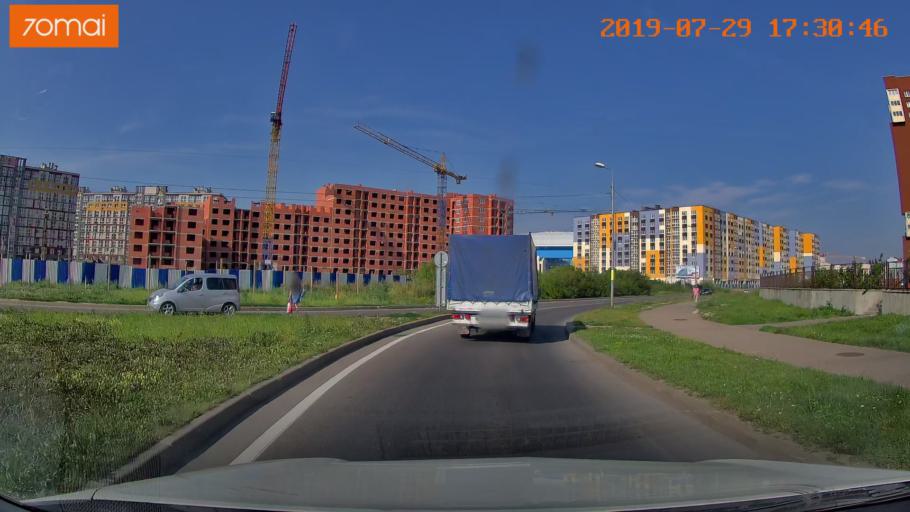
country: RU
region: Kaliningrad
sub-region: Gorod Kaliningrad
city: Kaliningrad
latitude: 54.7465
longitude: 20.4814
